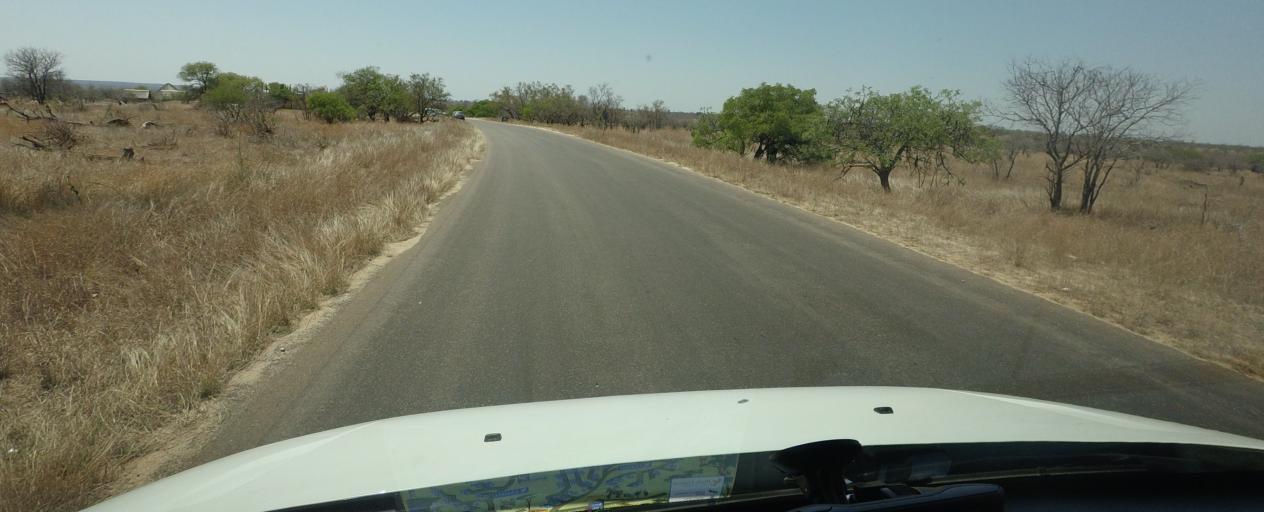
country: ZA
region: Limpopo
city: Thulamahashi
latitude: -24.4833
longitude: 31.3890
